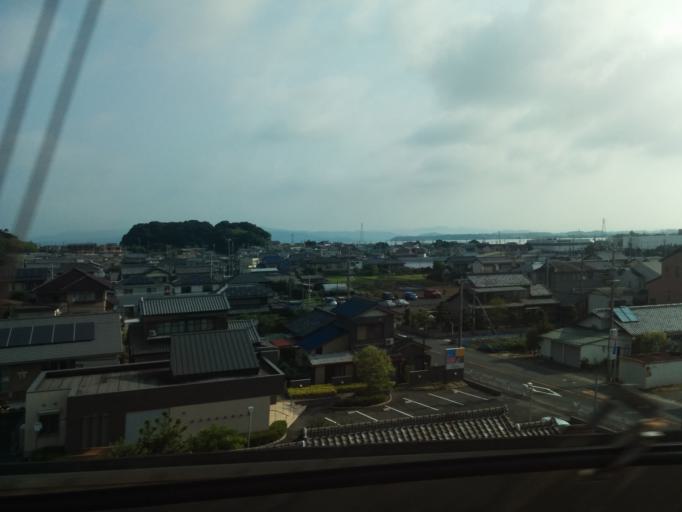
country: JP
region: Shizuoka
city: Kosai-shi
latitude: 34.6964
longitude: 137.5607
